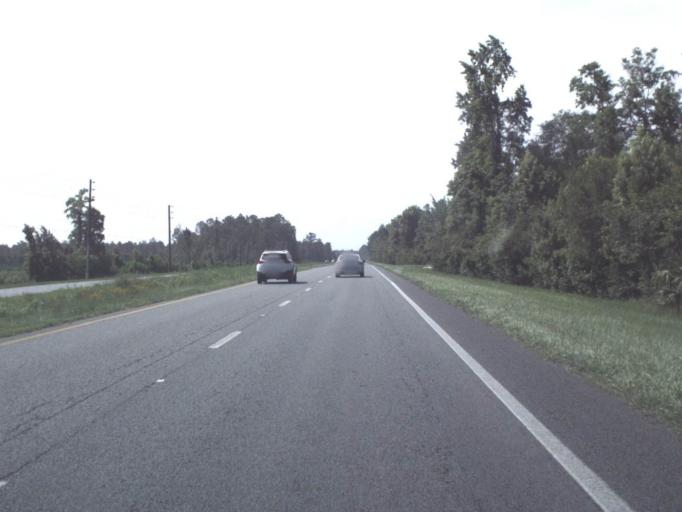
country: US
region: Florida
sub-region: Nassau County
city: Callahan
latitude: 30.6044
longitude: -81.8359
